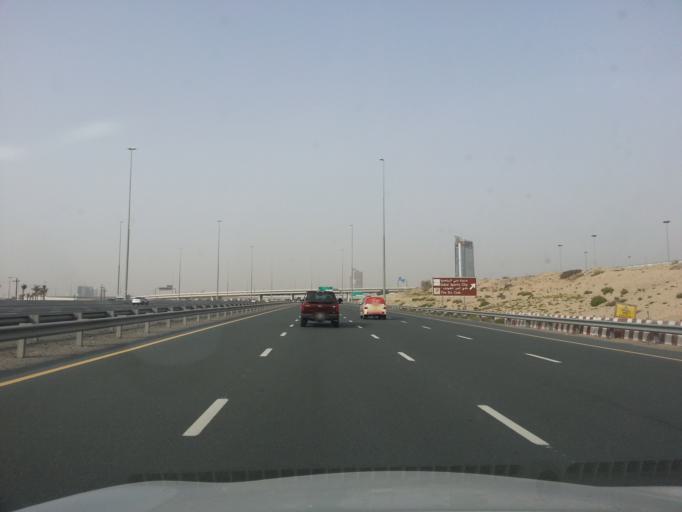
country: AE
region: Dubai
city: Dubai
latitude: 25.0485
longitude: 55.2170
